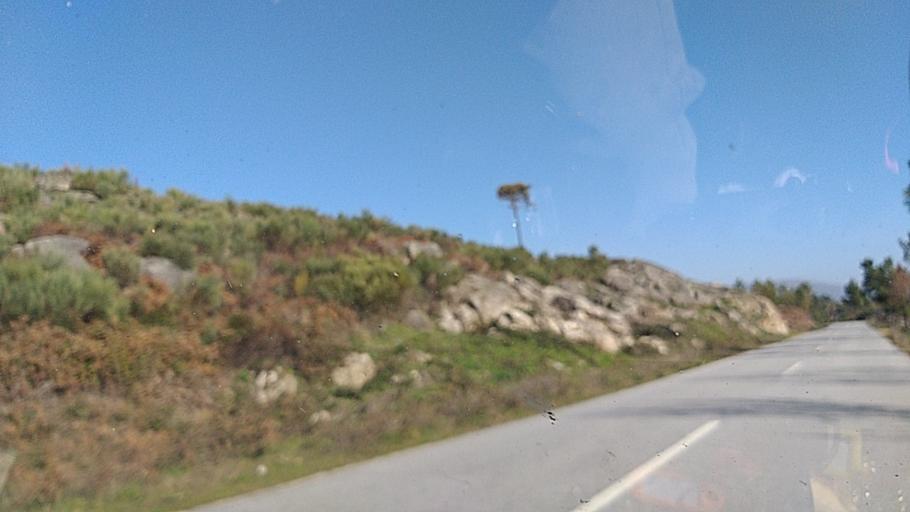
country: PT
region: Guarda
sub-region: Fornos de Algodres
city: Fornos de Algodres
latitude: 40.6432
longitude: -7.4733
